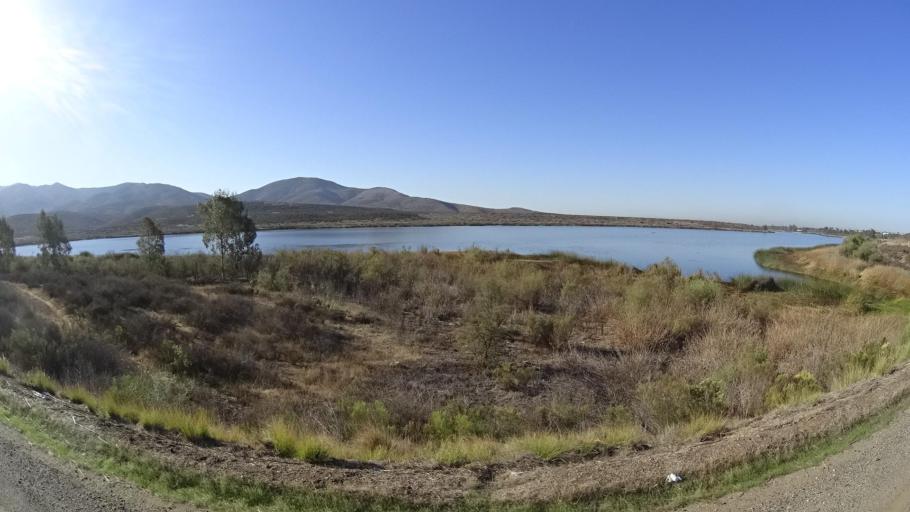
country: US
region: California
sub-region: San Diego County
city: Jamul
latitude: 32.6351
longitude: -116.9110
